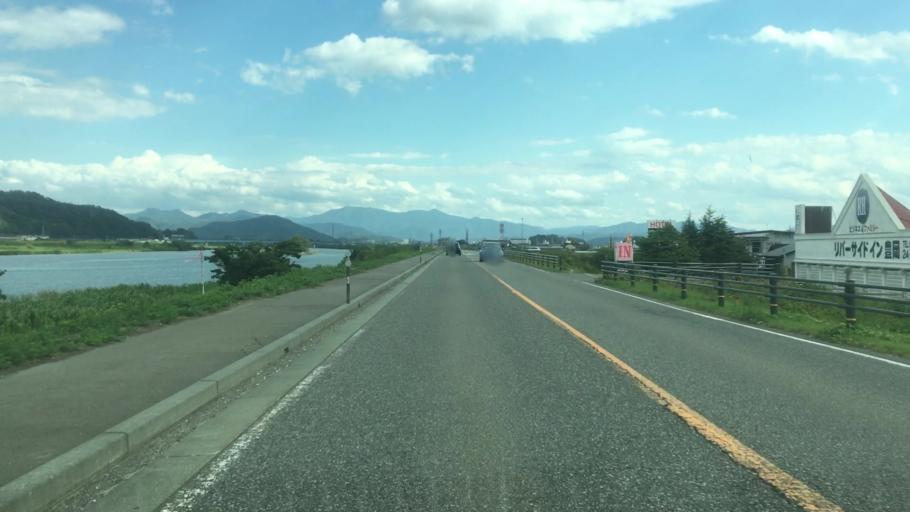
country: JP
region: Hyogo
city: Toyooka
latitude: 35.5699
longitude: 134.8089
